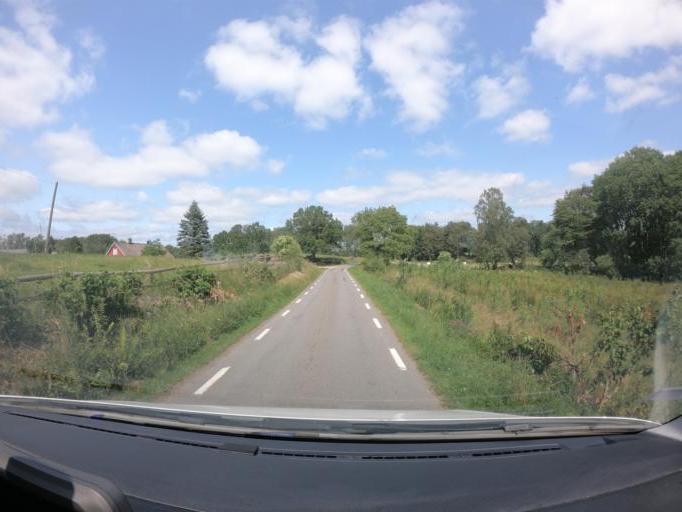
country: SE
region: Skane
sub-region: Hassleholms Kommun
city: Sosdala
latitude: 55.9683
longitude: 13.6612
